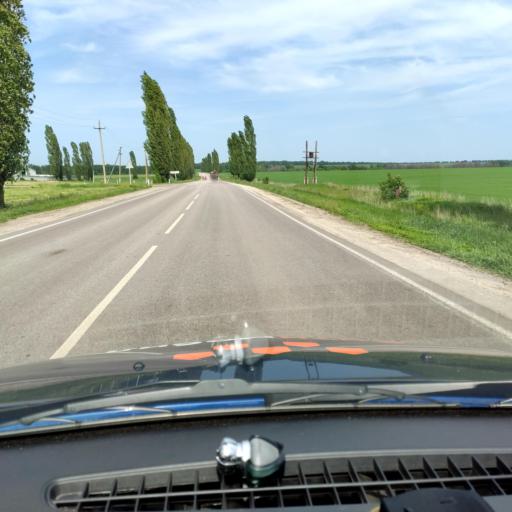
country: RU
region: Voronezj
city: Novaya Usman'
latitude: 51.5454
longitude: 39.3593
